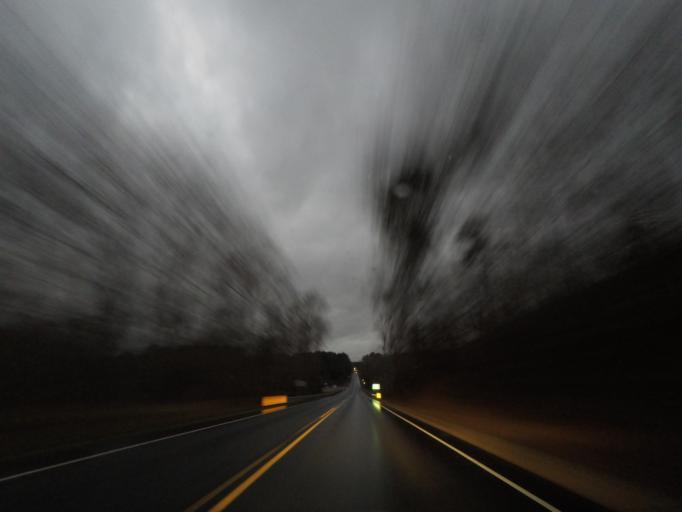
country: US
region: North Carolina
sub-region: Orange County
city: Hillsborough
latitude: 36.0748
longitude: -79.0698
